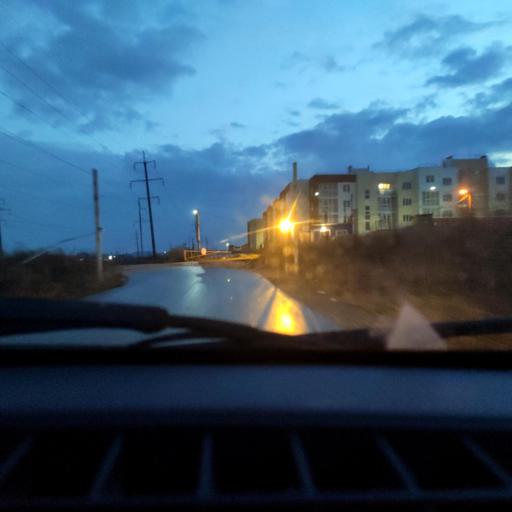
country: RU
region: Bashkortostan
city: Avdon
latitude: 54.7460
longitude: 55.7936
